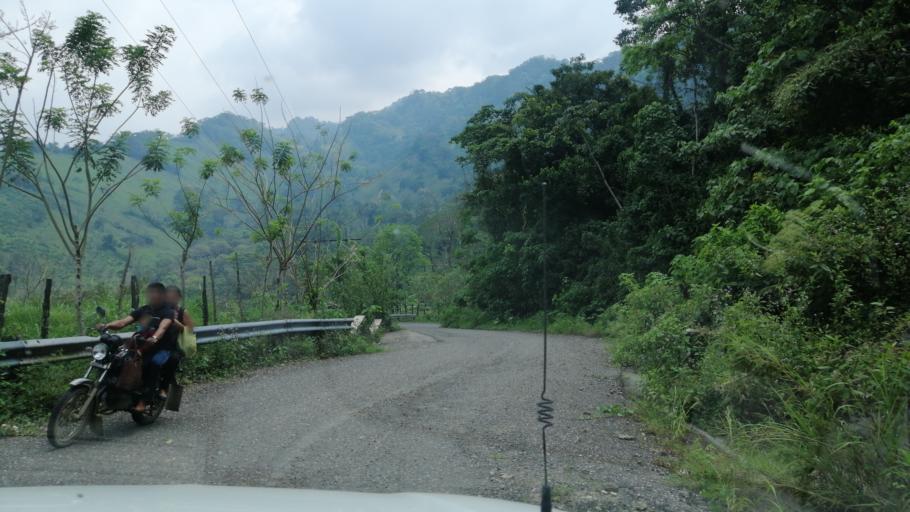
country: MX
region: Chiapas
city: Ostuacan
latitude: 17.3909
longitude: -93.3323
